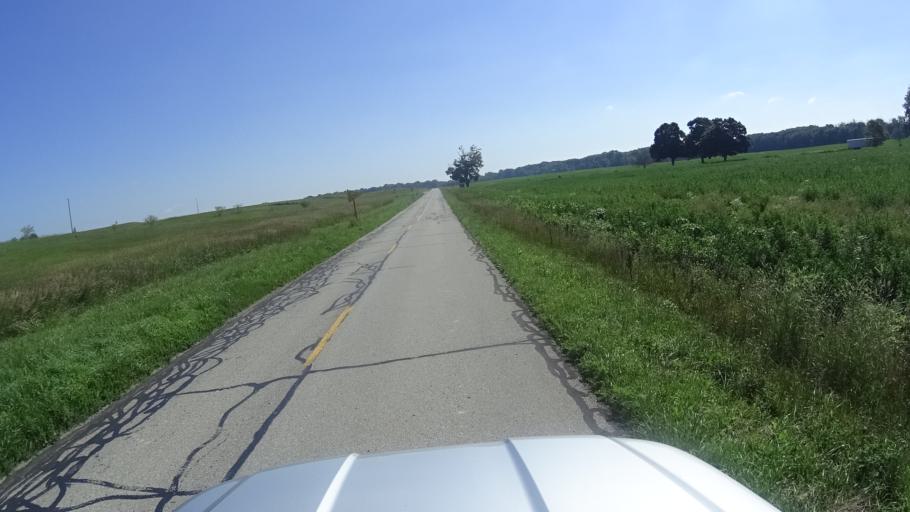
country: US
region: Indiana
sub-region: Madison County
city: Pendleton
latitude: 39.9875
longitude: -85.7728
